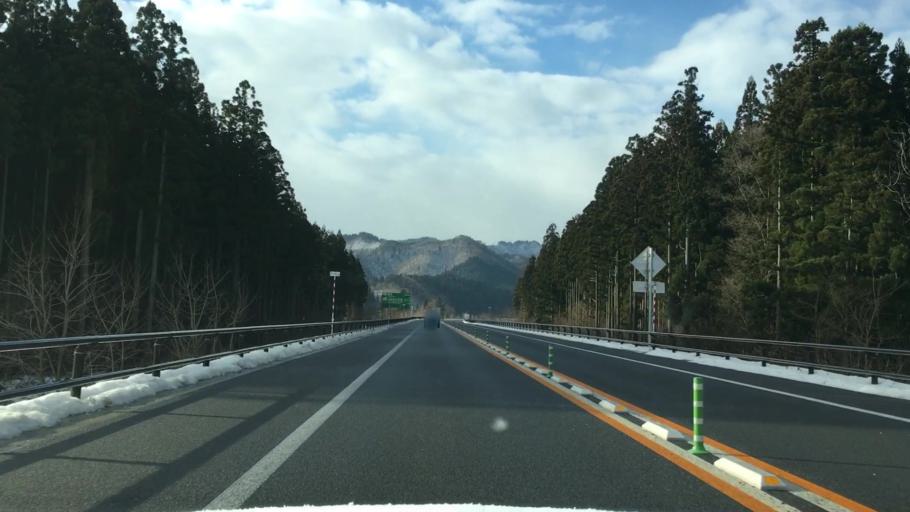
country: JP
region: Akita
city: Odate
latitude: 40.2413
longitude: 140.5067
